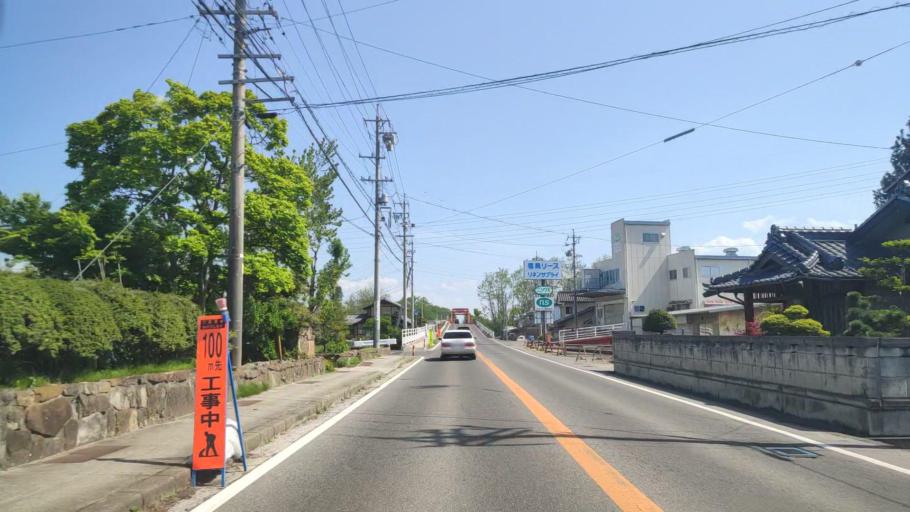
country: JP
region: Nagano
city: Hotaka
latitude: 36.3542
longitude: 137.8811
